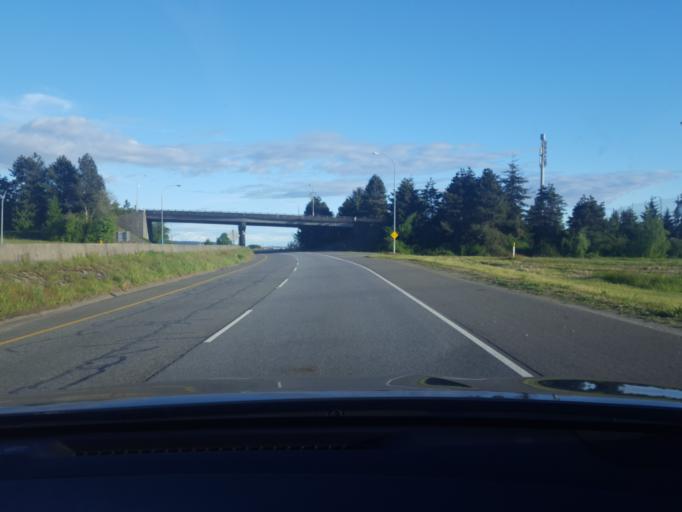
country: CA
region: British Columbia
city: Delta
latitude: 49.1208
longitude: -122.9276
